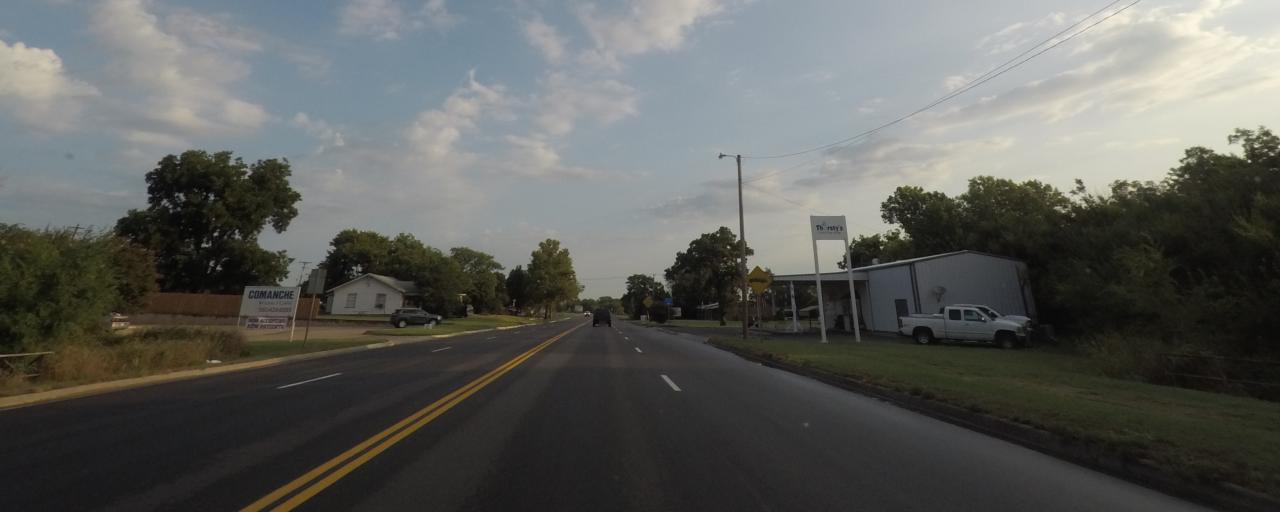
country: US
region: Oklahoma
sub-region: Stephens County
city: Comanche
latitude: 34.3708
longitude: -97.9642
